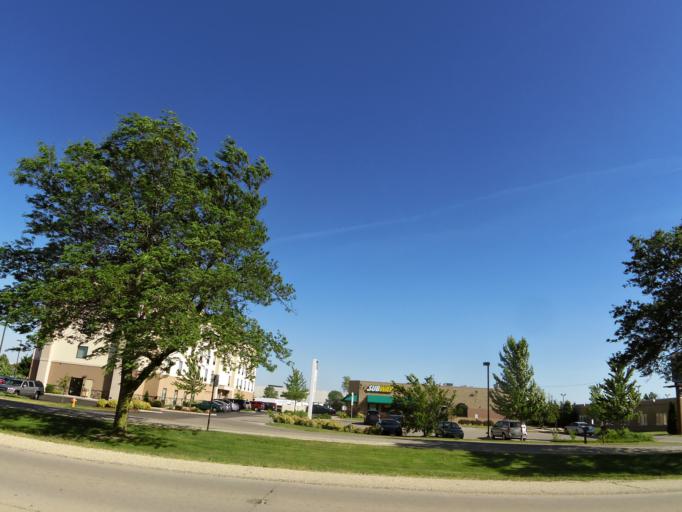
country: US
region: Wisconsin
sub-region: Rock County
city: Beloit
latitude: 42.5232
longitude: -88.9864
